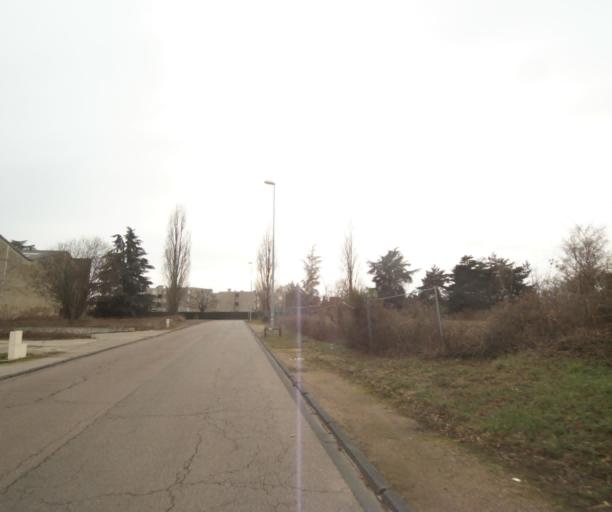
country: FR
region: Rhone-Alpes
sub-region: Departement de la Loire
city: Roanne
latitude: 46.0569
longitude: 4.0788
